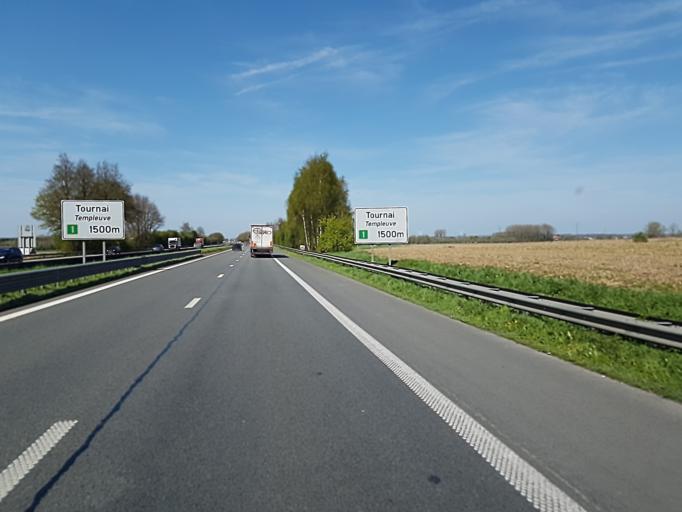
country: BE
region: Wallonia
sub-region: Province du Hainaut
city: Pecq
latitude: 50.6332
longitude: 3.3088
